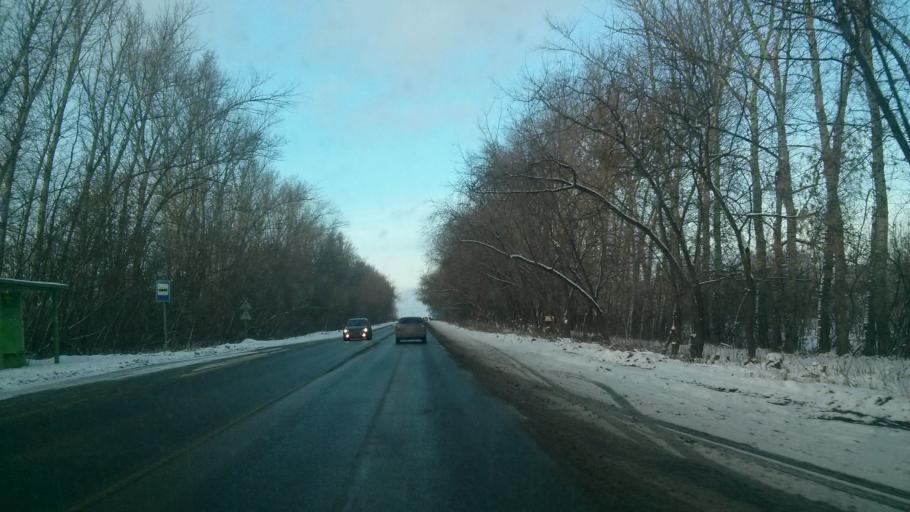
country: RU
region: Vladimir
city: Murom
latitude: 55.6082
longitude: 42.0260
